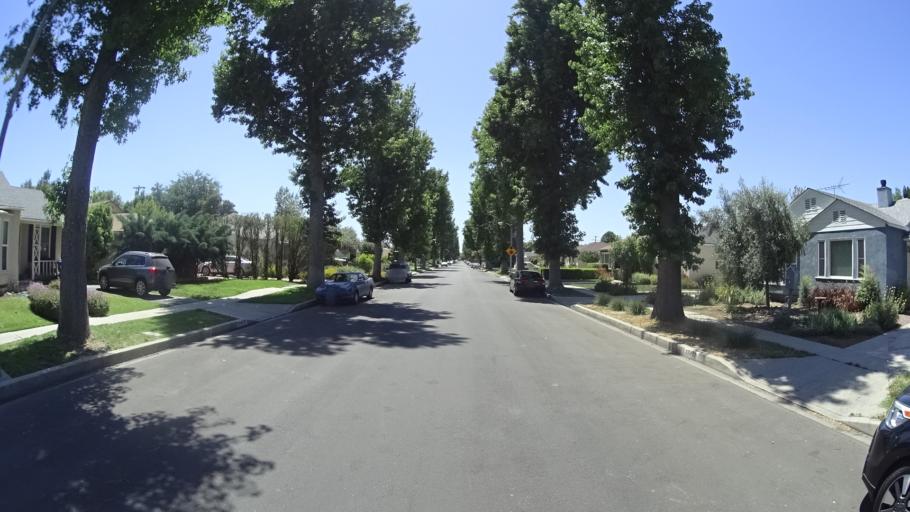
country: US
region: California
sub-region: Los Angeles County
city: Northridge
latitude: 34.1876
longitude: -118.5125
